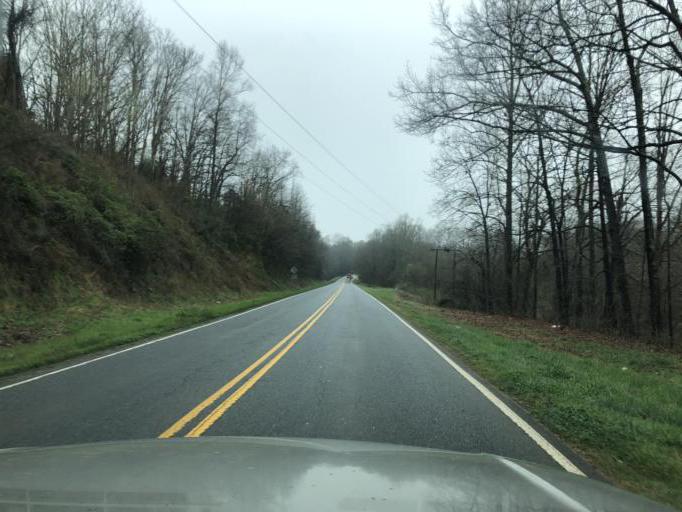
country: US
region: North Carolina
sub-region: Cleveland County
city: Shelby
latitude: 35.3263
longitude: -81.4714
